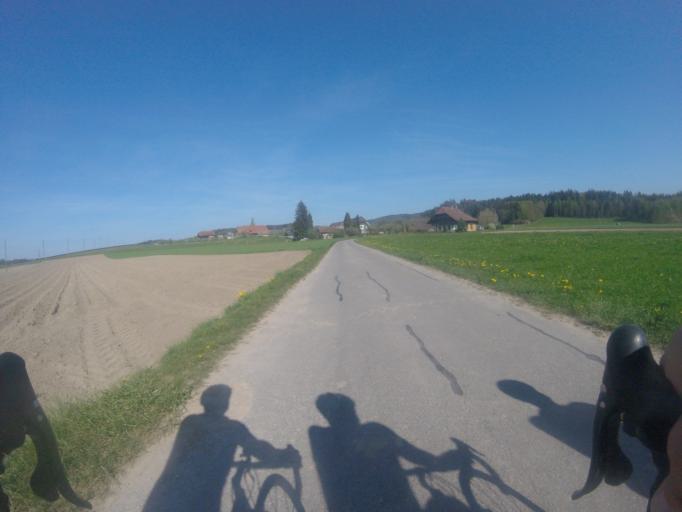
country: CH
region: Bern
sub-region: Bern-Mittelland District
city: Wohlen
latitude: 46.9709
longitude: 7.3444
